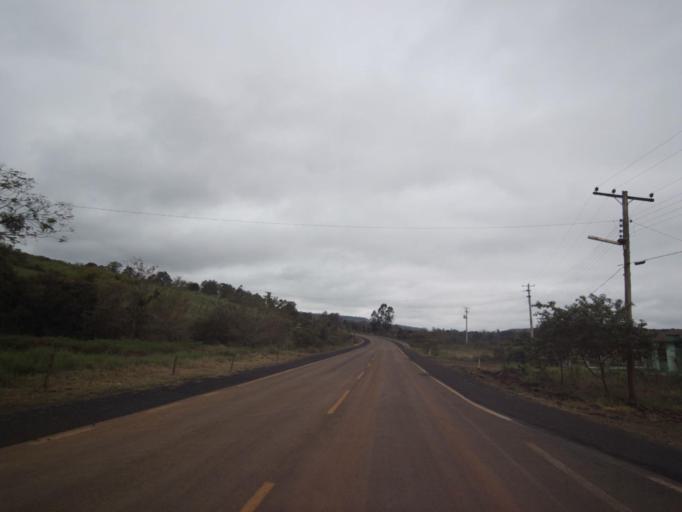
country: AR
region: Misiones
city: El Soberbio
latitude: -27.2916
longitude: -54.1905
